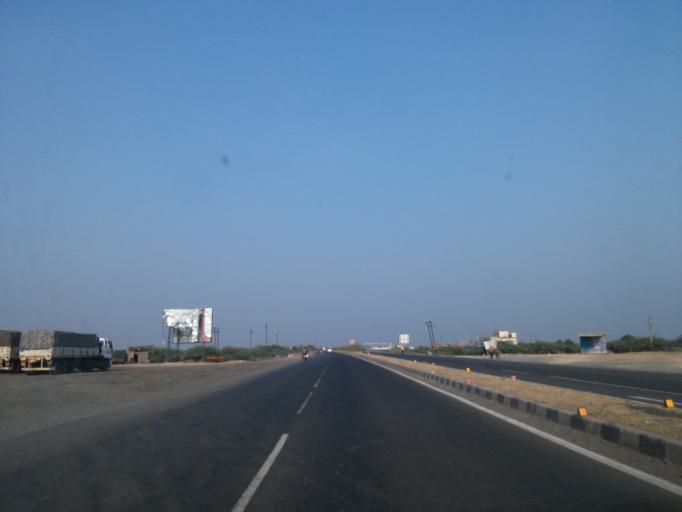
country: IN
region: Gujarat
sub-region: Surendranagar
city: Lakhtar
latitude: 23.0503
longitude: 71.7128
